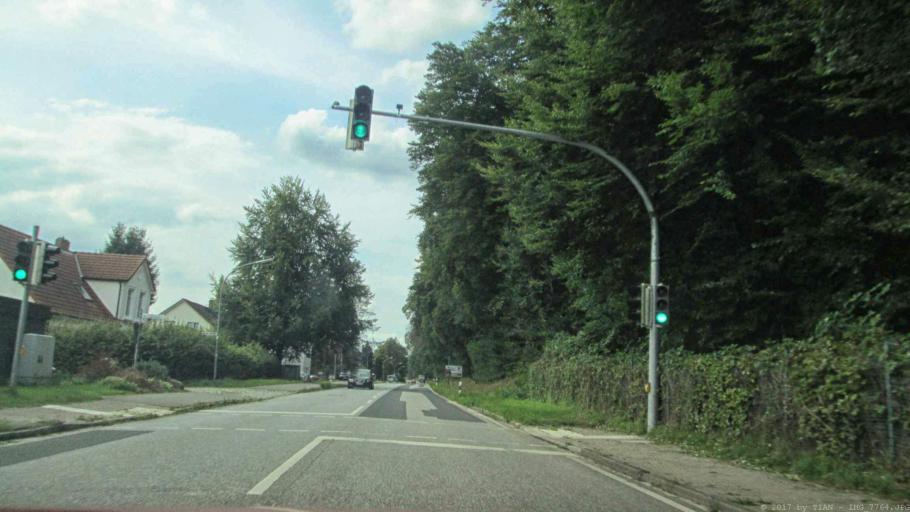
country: DE
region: Schleswig-Holstein
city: Bornsen
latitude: 53.4675
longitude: 10.2870
